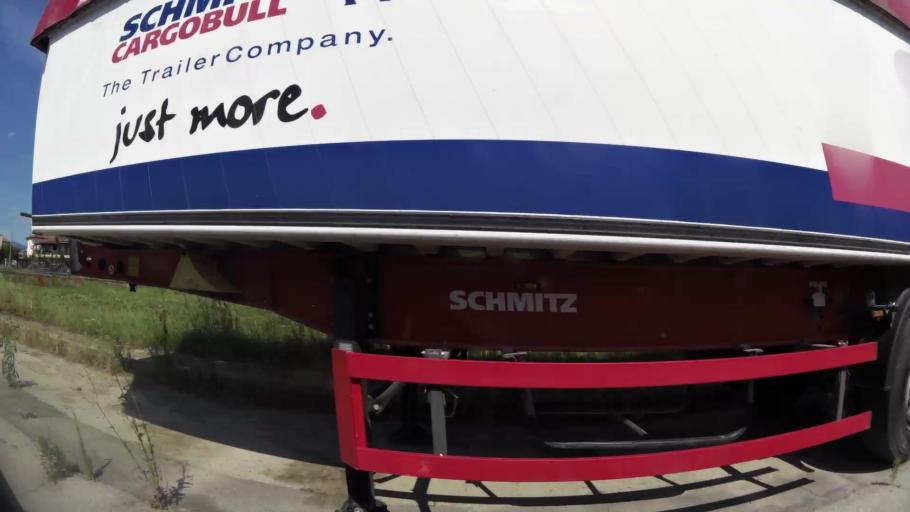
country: GR
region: Central Macedonia
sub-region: Nomos Pierias
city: Katerini
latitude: 40.2774
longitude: 22.4898
